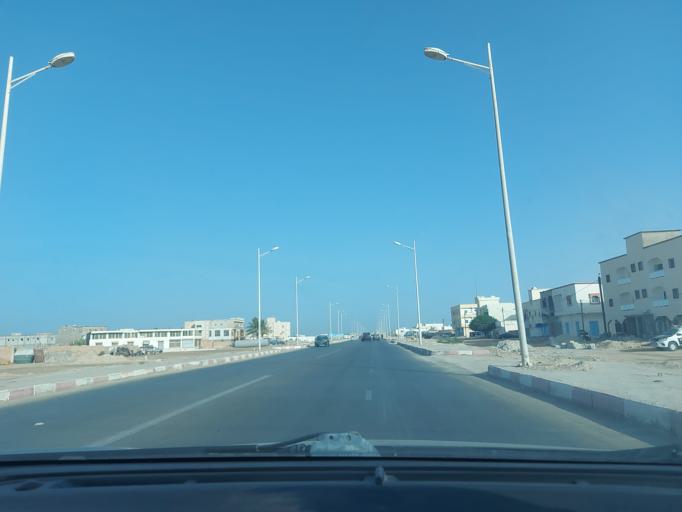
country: MR
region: Nouakchott
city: Nouakchott
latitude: 18.0934
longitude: -16.0130
